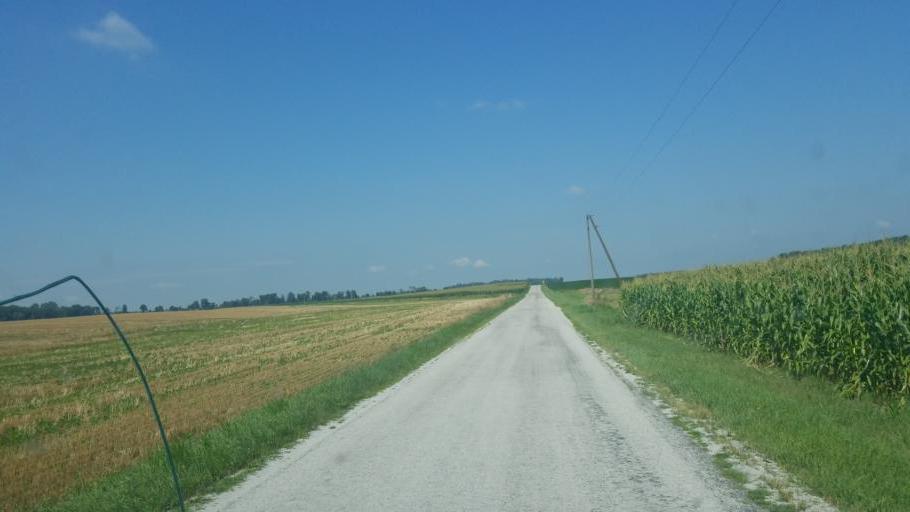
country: US
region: Ohio
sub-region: Hardin County
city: Kenton
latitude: 40.6750
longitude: -83.6279
